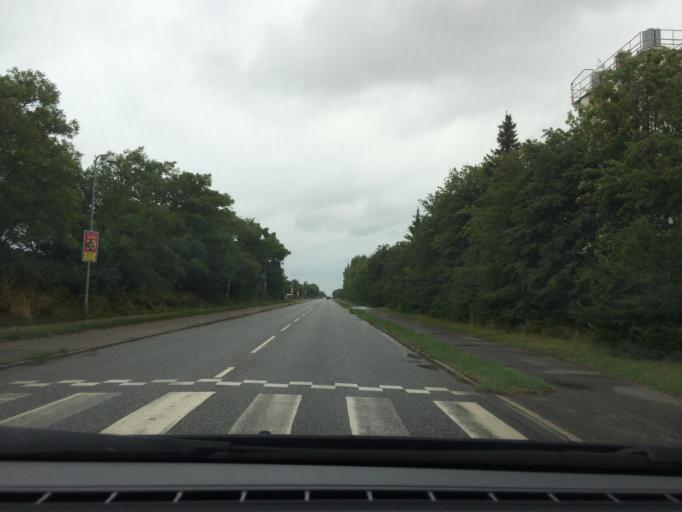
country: DK
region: Zealand
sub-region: Vordingborg Kommune
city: Stege
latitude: 54.9943
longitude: 12.2840
